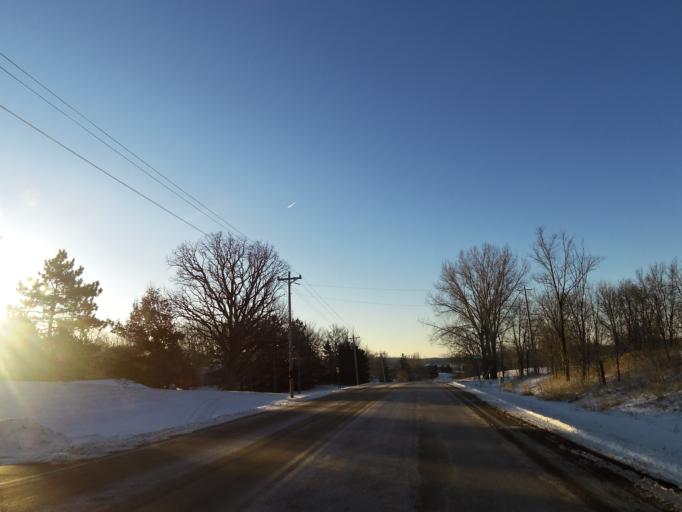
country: US
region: Minnesota
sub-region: Scott County
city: Prior Lake
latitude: 44.6609
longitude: -93.4603
